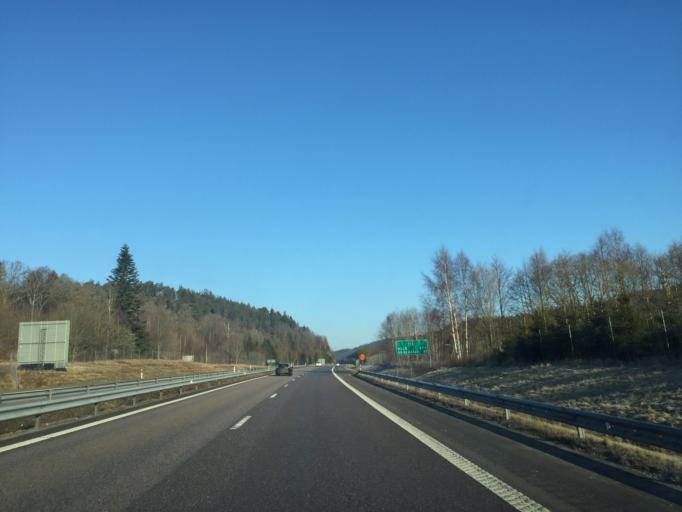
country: SE
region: Vaestra Goetaland
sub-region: Uddevalla Kommun
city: Ljungskile
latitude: 58.2355
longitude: 11.9117
